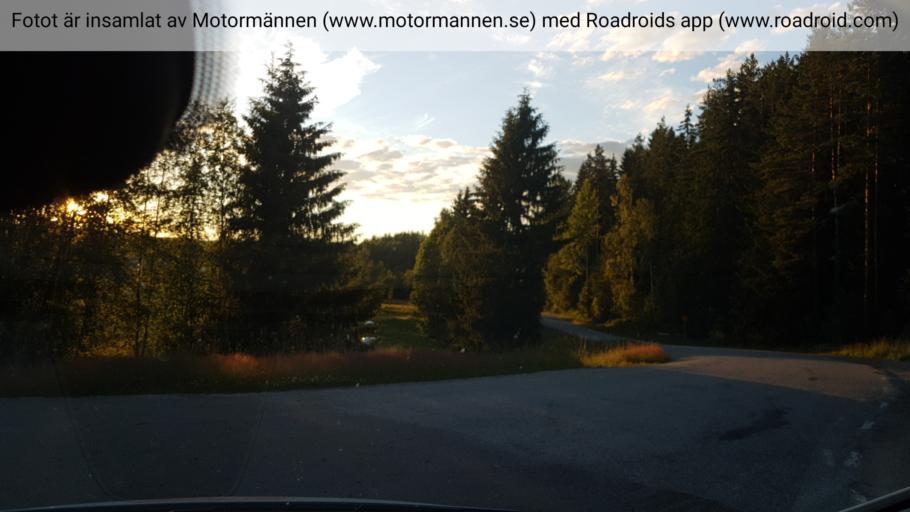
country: SE
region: Vaermland
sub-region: Sunne Kommun
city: Sunne
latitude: 59.6670
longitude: 12.9101
